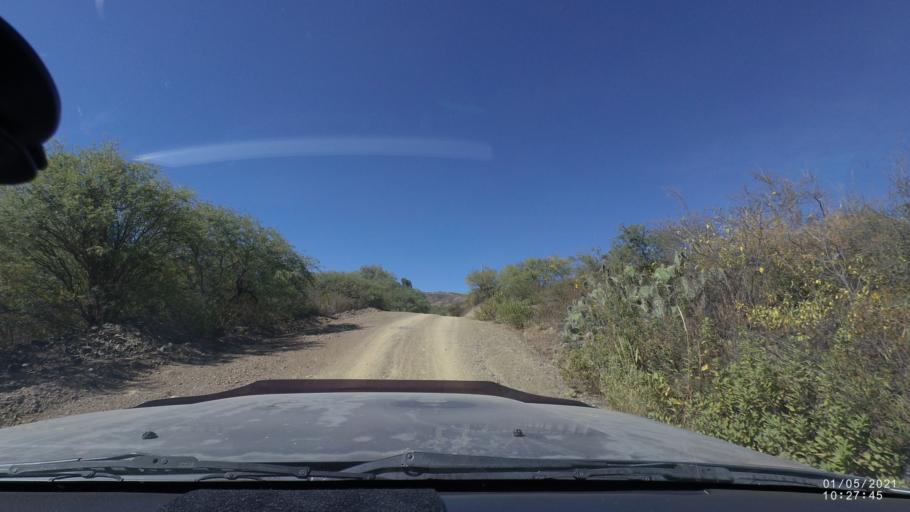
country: BO
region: Cochabamba
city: Capinota
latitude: -17.5864
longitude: -66.1905
